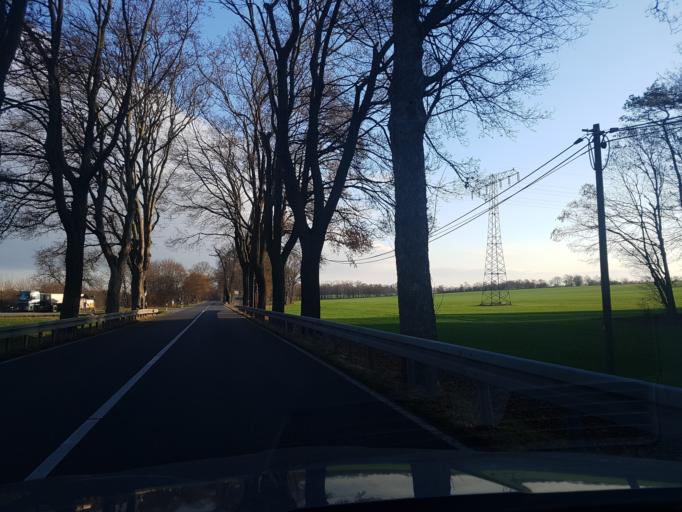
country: DE
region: Brandenburg
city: Luckau
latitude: 51.8260
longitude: 13.6191
